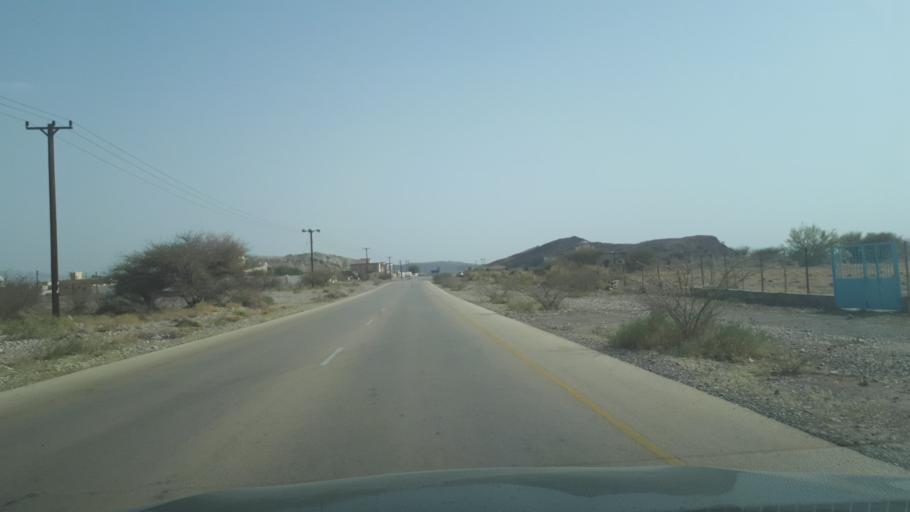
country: OM
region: Az Zahirah
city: `Ibri
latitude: 23.1600
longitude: 56.9121
